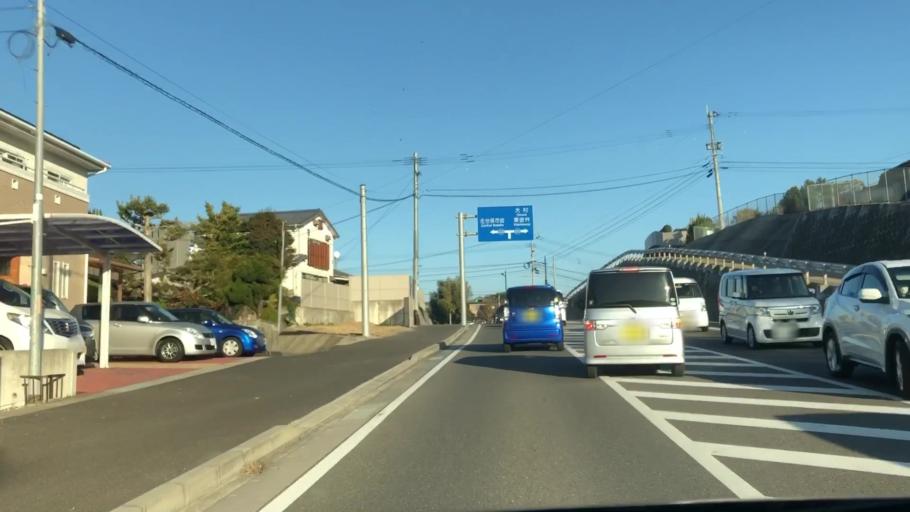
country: JP
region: Nagasaki
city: Sasebo
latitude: 33.1272
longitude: 129.7971
